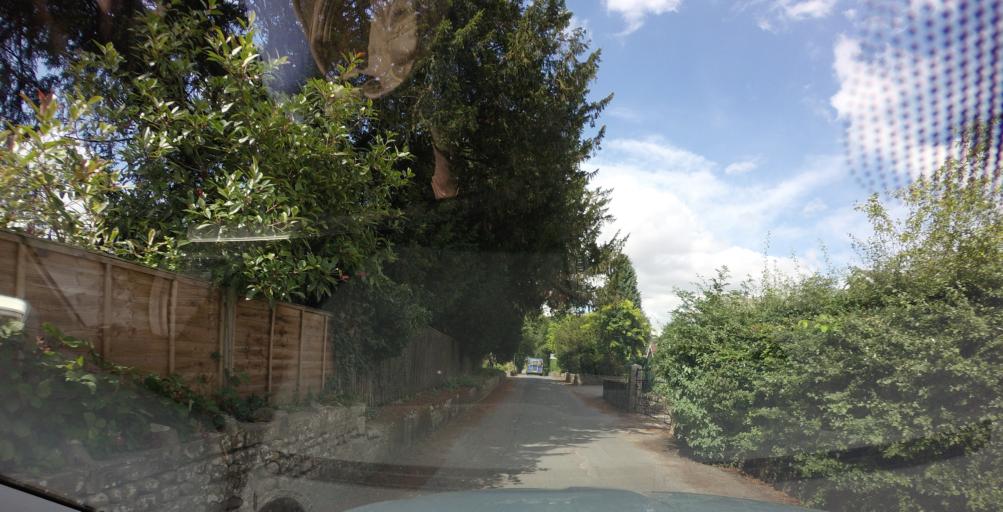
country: GB
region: England
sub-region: North Yorkshire
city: Ripon
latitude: 54.1403
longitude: -1.4960
